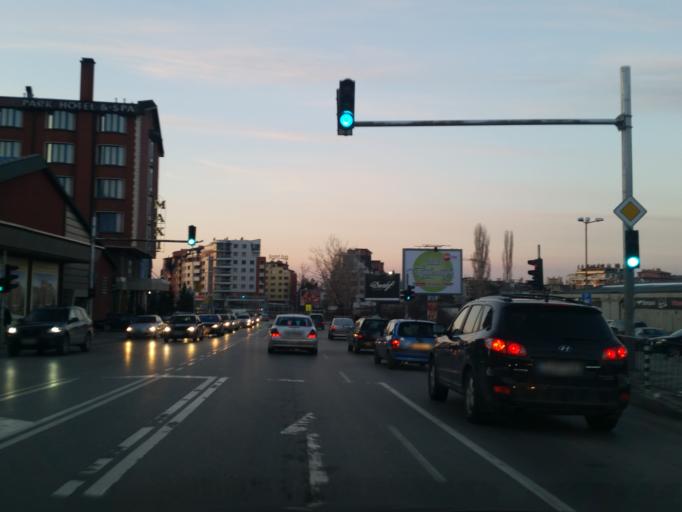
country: BG
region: Sofia-Capital
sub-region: Stolichna Obshtina
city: Sofia
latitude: 42.6406
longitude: 23.3346
